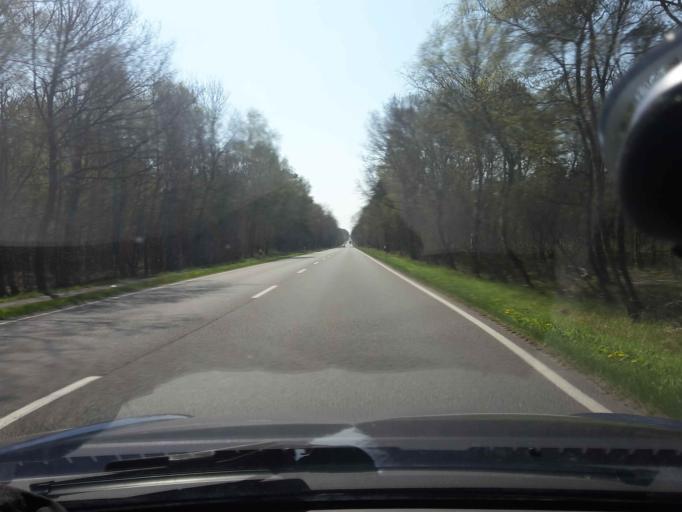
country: DE
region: Lower Saxony
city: Schneverdingen
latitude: 53.1080
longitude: 9.8537
